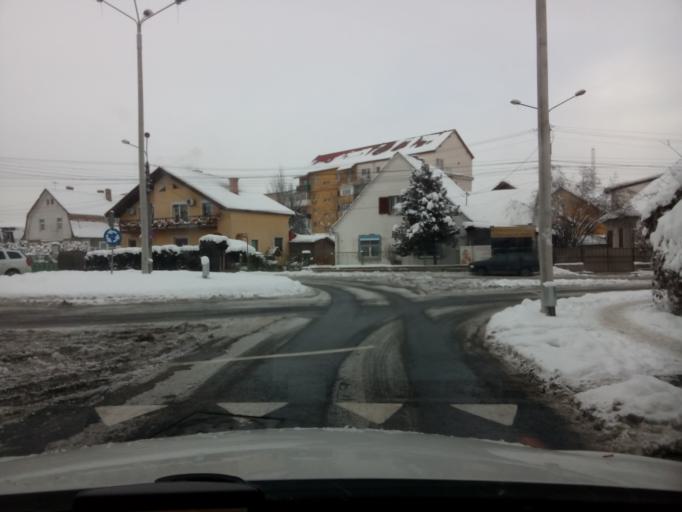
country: RO
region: Sibiu
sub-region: Municipiul Sibiu
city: Sibiu
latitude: 45.7909
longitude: 24.1385
